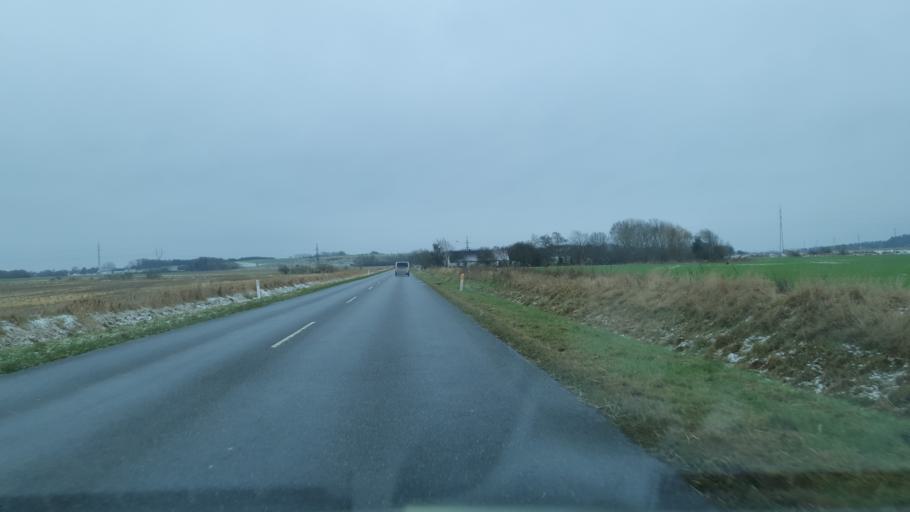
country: DK
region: North Denmark
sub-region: Jammerbugt Kommune
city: Brovst
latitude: 57.1202
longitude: 9.4949
